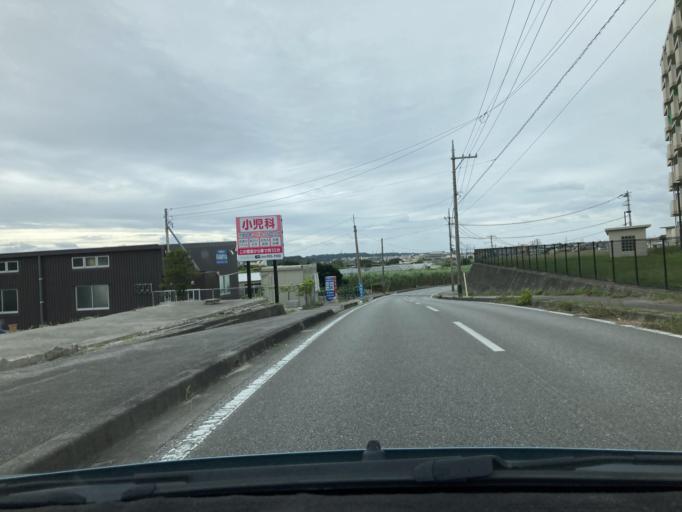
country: JP
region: Okinawa
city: Tomigusuku
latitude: 26.1522
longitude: 127.6971
